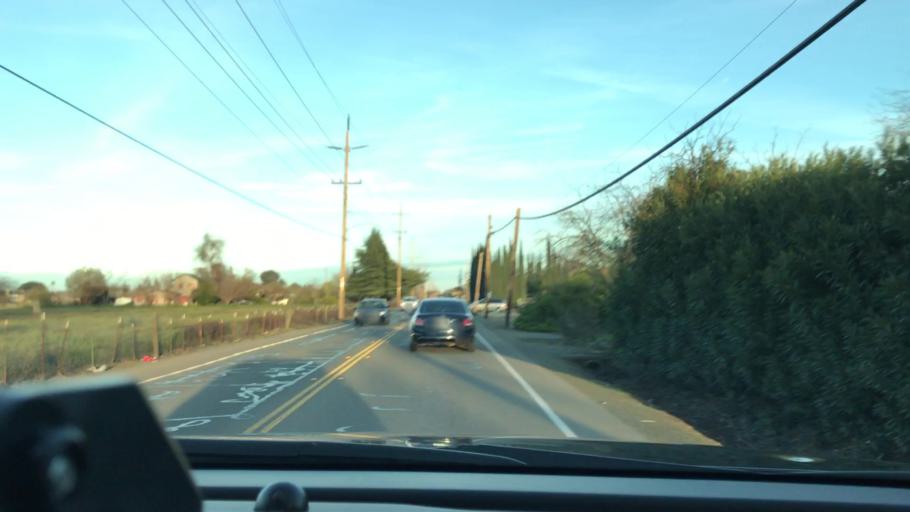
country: US
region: California
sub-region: Contra Costa County
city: Brentwood
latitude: 37.9616
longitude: -121.7116
